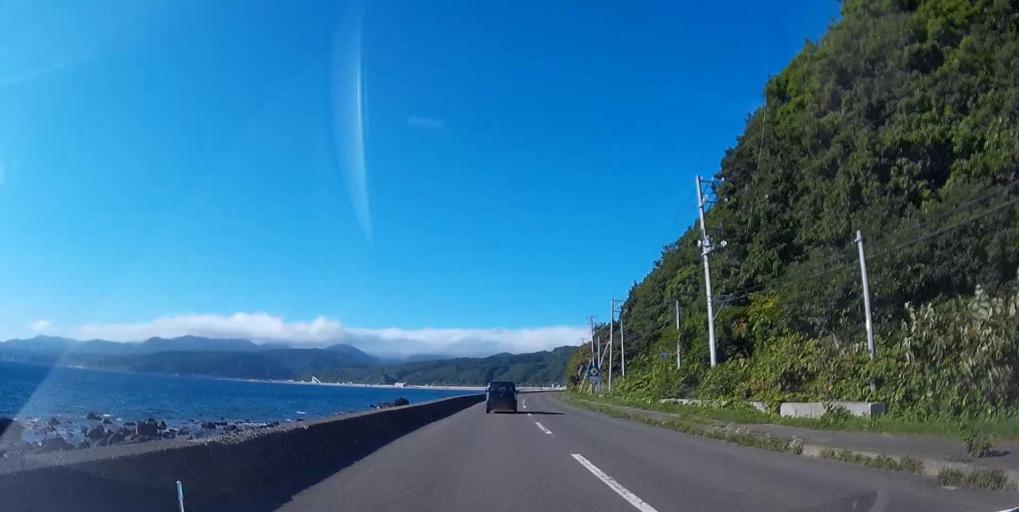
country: JP
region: Hokkaido
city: Kamiiso
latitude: 42.1977
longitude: 139.8805
